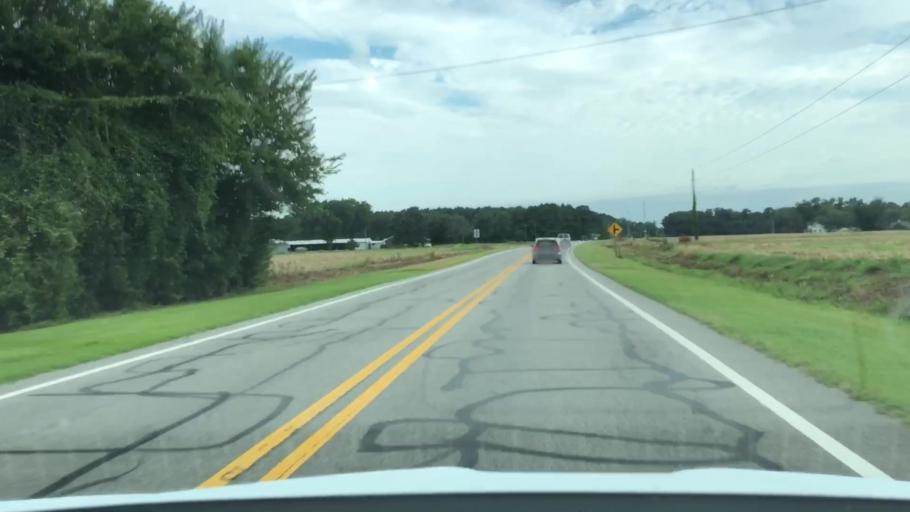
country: US
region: North Carolina
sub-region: Lenoir County
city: Kinston
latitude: 35.1590
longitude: -77.5544
